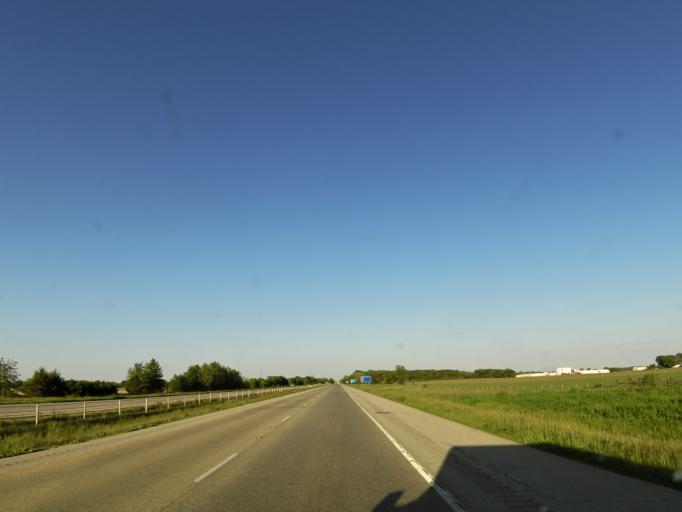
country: US
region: Illinois
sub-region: Champaign County
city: Saint Joseph
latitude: 40.1205
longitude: -88.0808
